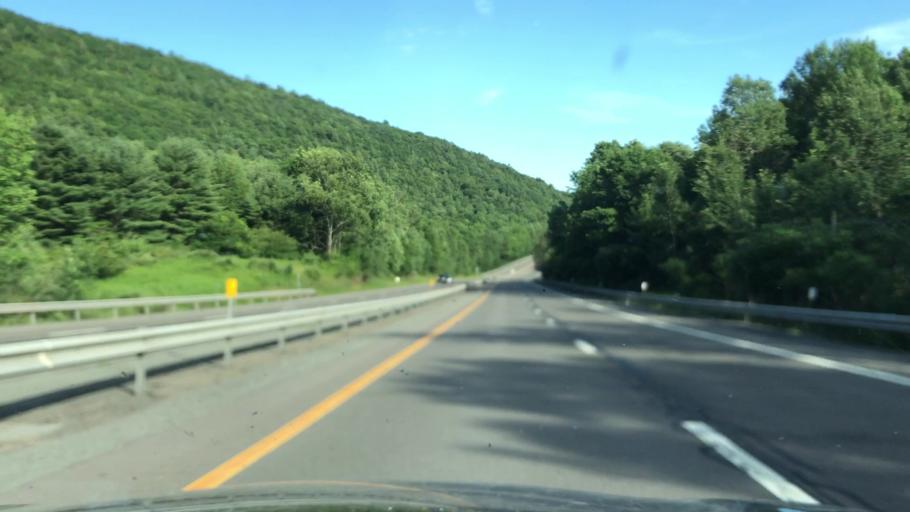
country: US
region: New York
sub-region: Delaware County
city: Hancock
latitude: 41.9661
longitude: -75.3232
